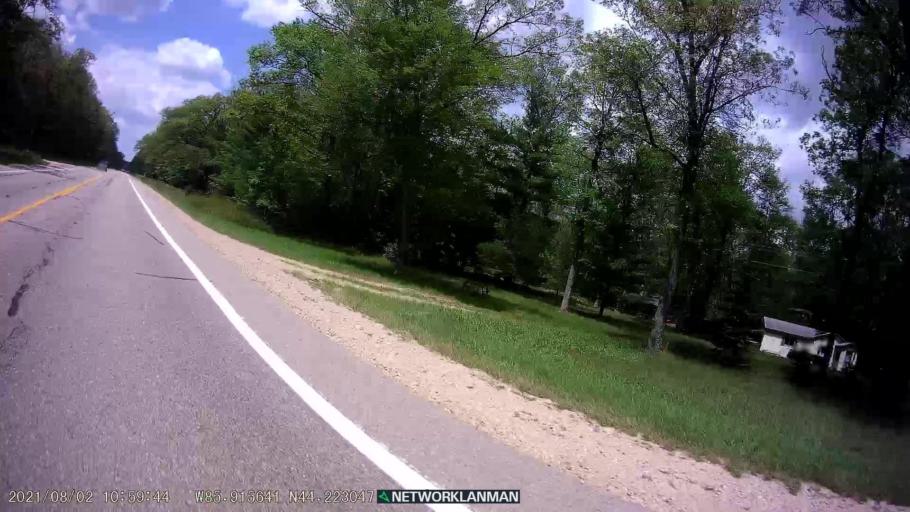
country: US
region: Michigan
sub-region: Lake County
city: Baldwin
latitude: 44.2231
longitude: -85.9162
